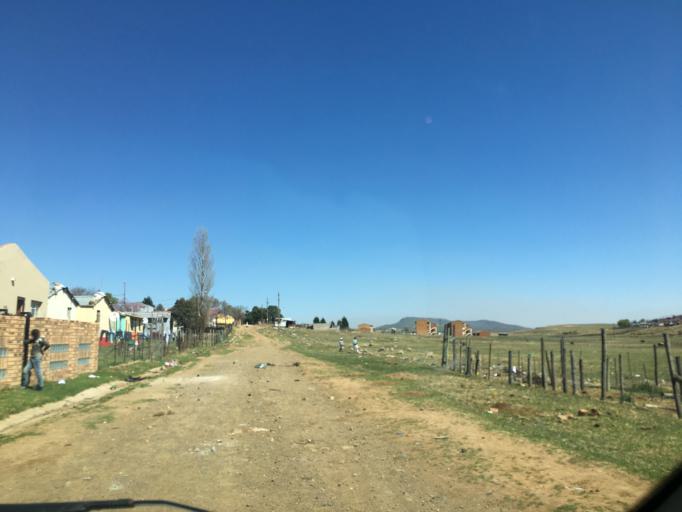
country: ZA
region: Eastern Cape
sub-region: Chris Hani District Municipality
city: Elliot
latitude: -31.3270
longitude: 27.8262
